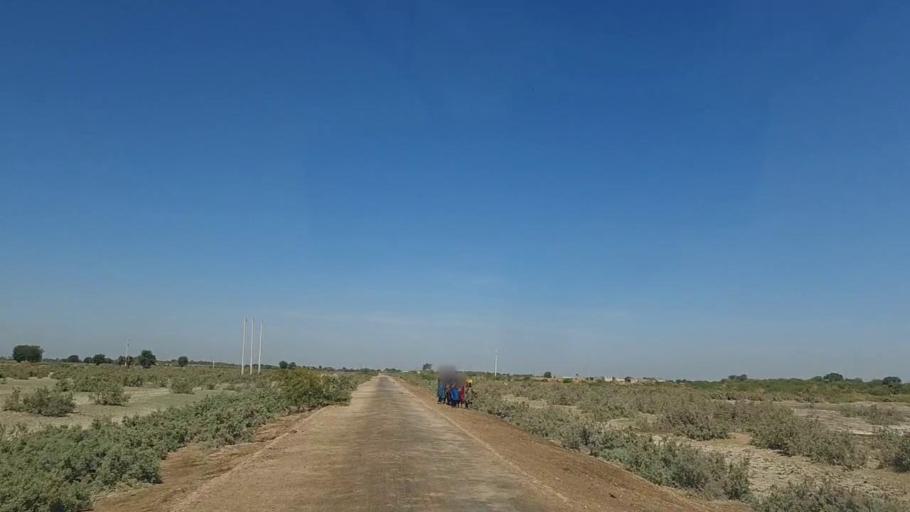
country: PK
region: Sindh
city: Samaro
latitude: 25.3009
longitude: 69.4858
